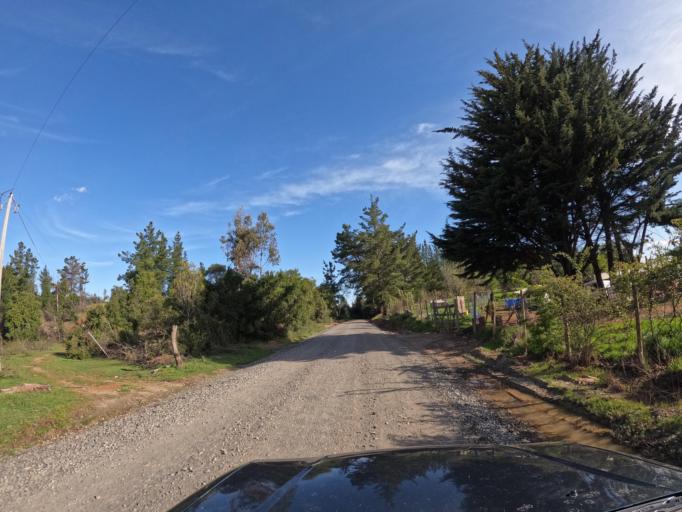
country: CL
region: Biobio
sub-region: Provincia de Biobio
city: La Laja
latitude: -37.1545
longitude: -72.7263
